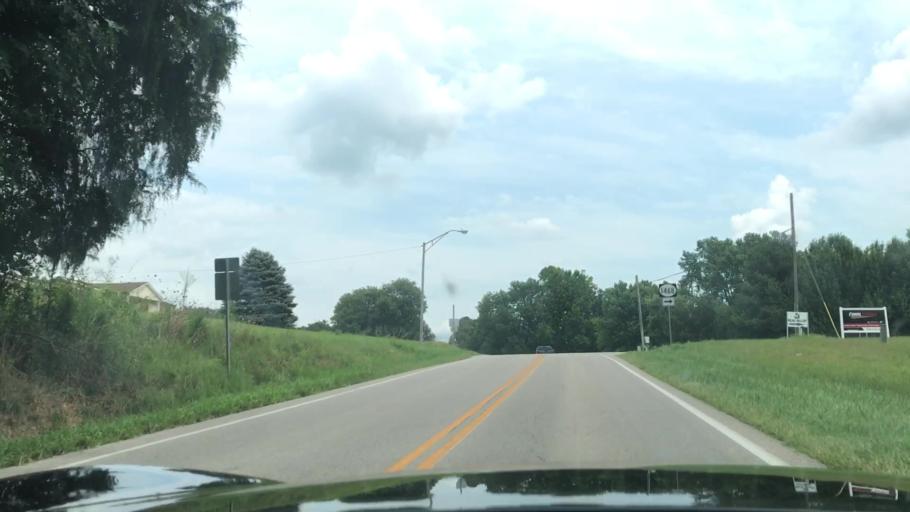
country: US
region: Kentucky
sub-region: Butler County
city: Morgantown
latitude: 37.2105
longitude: -86.7191
